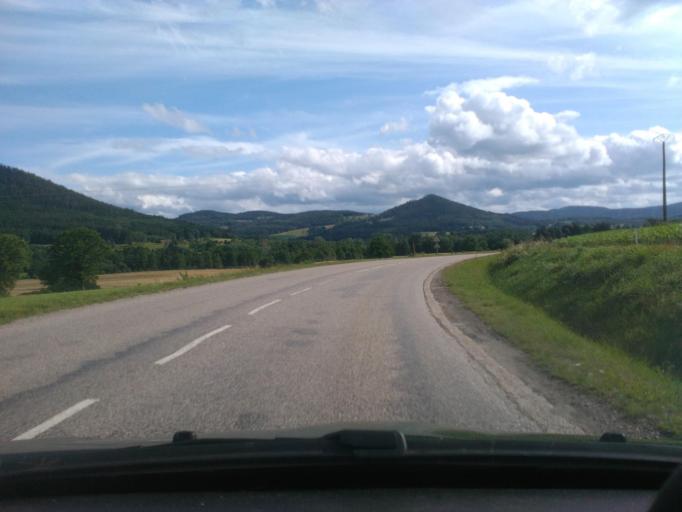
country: FR
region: Lorraine
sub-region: Departement des Vosges
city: Granges-sur-Vologne
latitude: 48.2063
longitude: 6.8022
